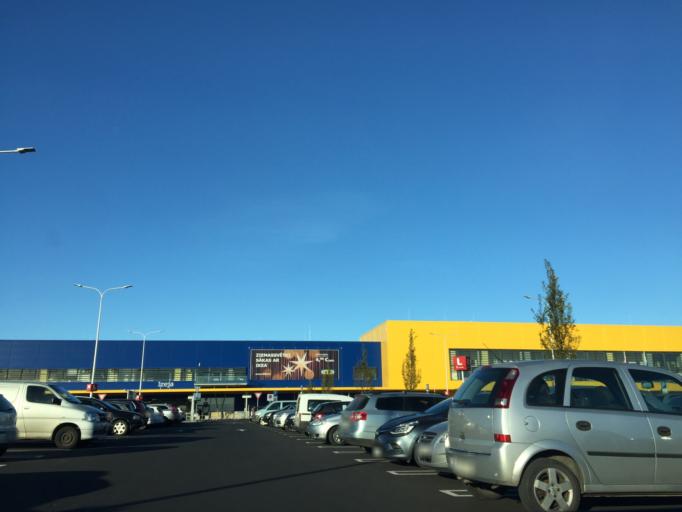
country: LV
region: Stopini
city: Ulbroka
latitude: 56.9533
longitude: 24.2542
